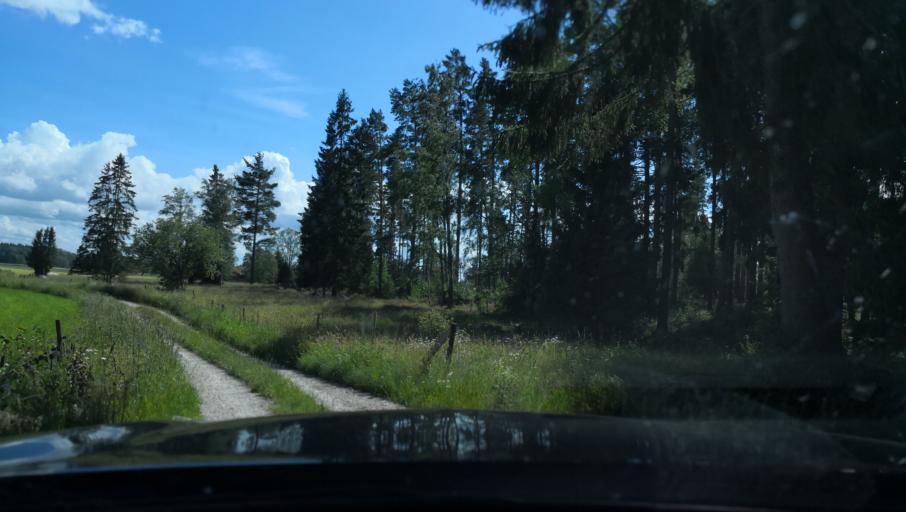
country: SE
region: Vaestmanland
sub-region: Kungsors Kommun
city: Kungsoer
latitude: 59.3289
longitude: 16.0651
